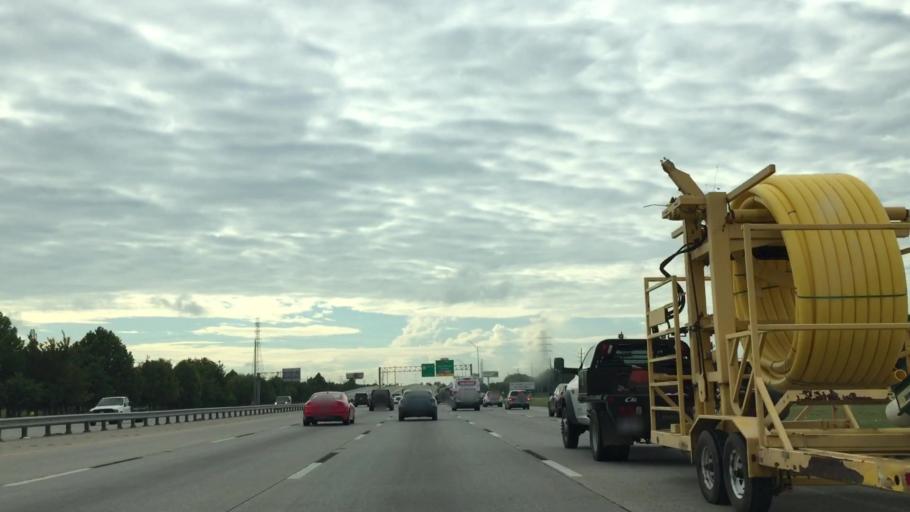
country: US
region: Texas
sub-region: Harris County
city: Hudson
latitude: 29.9483
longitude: -95.5320
